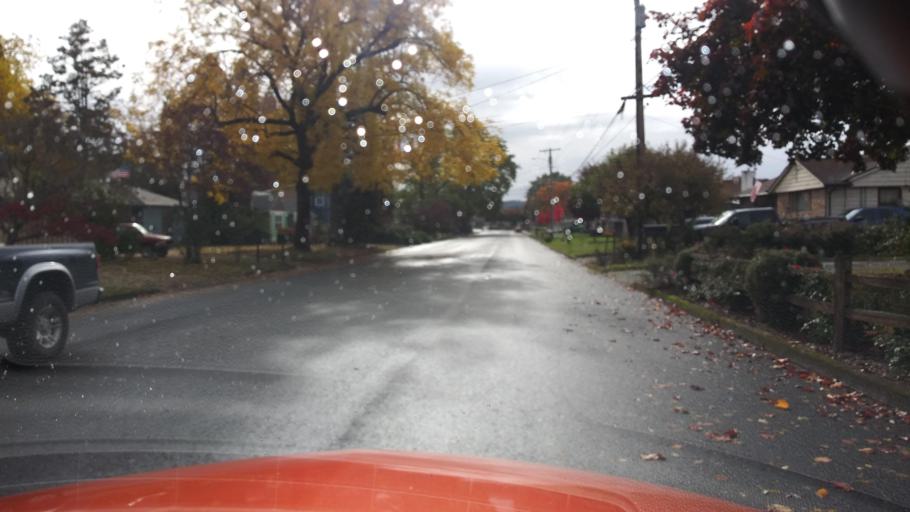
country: US
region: Oregon
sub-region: Washington County
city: Forest Grove
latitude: 45.5223
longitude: -123.0925
